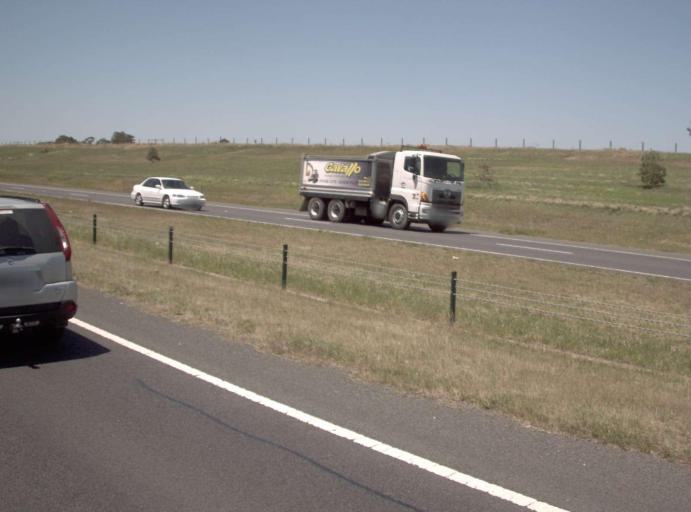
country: AU
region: Victoria
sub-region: Cardinia
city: Officer South
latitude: -38.0658
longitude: 145.3760
